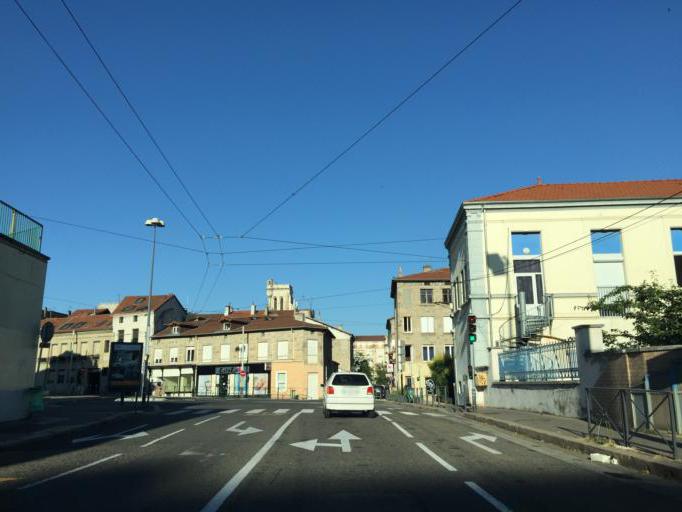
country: FR
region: Rhone-Alpes
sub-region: Departement de la Loire
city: Saint-Etienne
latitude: 45.4302
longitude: 4.3955
